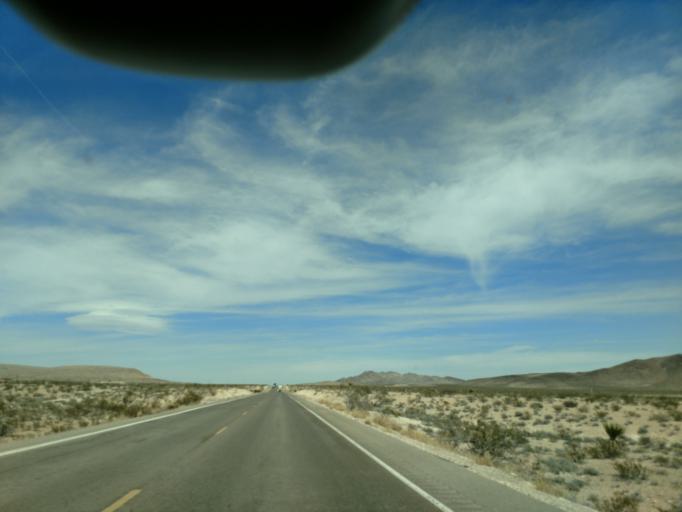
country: US
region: Nevada
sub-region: Clark County
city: Enterprise
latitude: 35.8478
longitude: -115.2635
